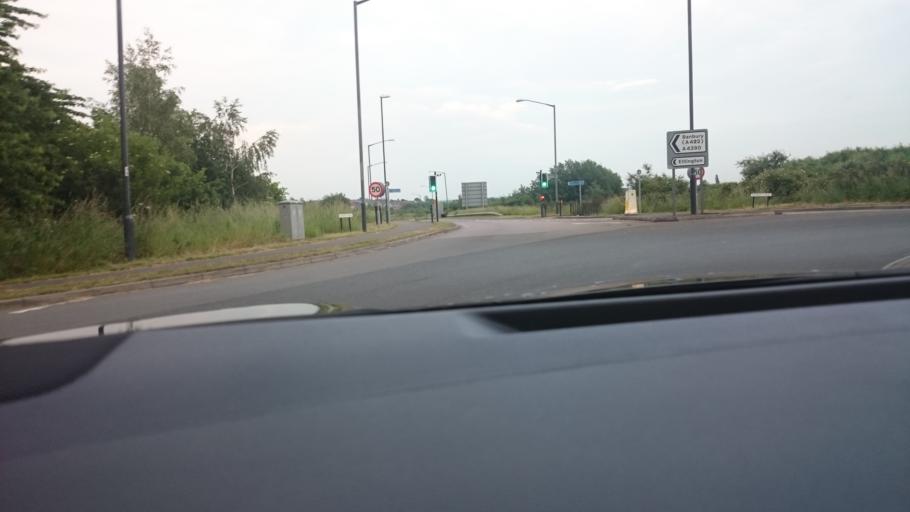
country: GB
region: England
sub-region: Warwickshire
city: Stratford-upon-Avon
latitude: 52.1812
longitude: -1.7005
